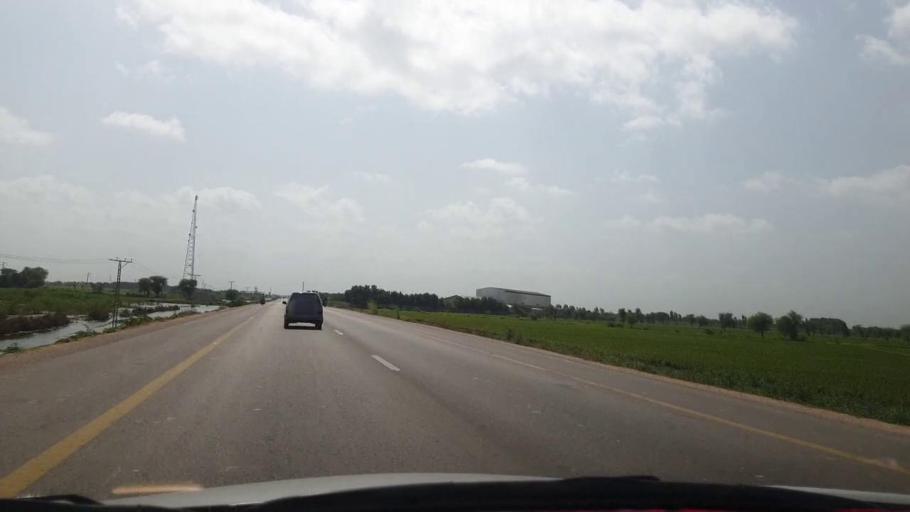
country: PK
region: Sindh
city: Matli
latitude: 24.9379
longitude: 68.7065
